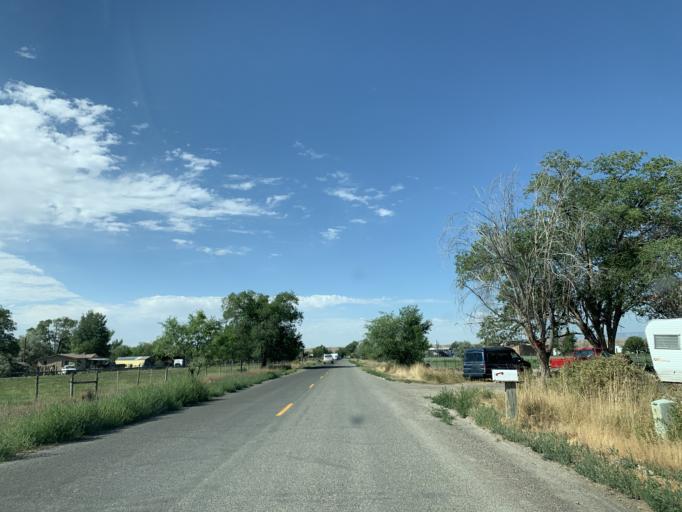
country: US
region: Utah
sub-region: Carbon County
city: Wellington
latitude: 39.5456
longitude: -110.6862
